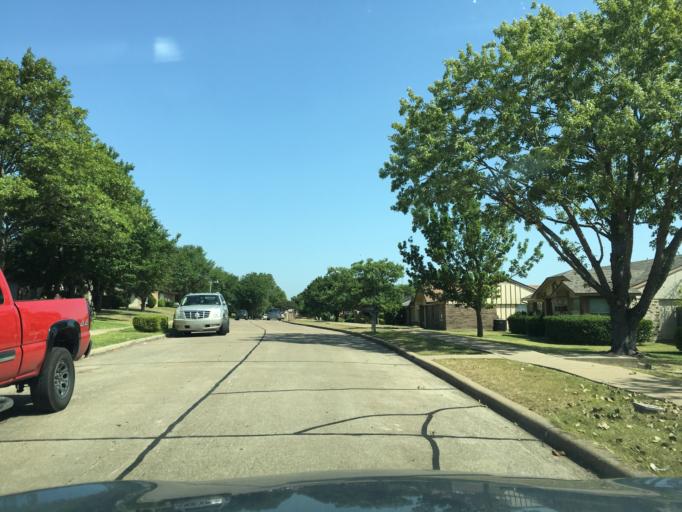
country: US
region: Texas
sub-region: Dallas County
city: Garland
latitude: 32.8885
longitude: -96.6173
